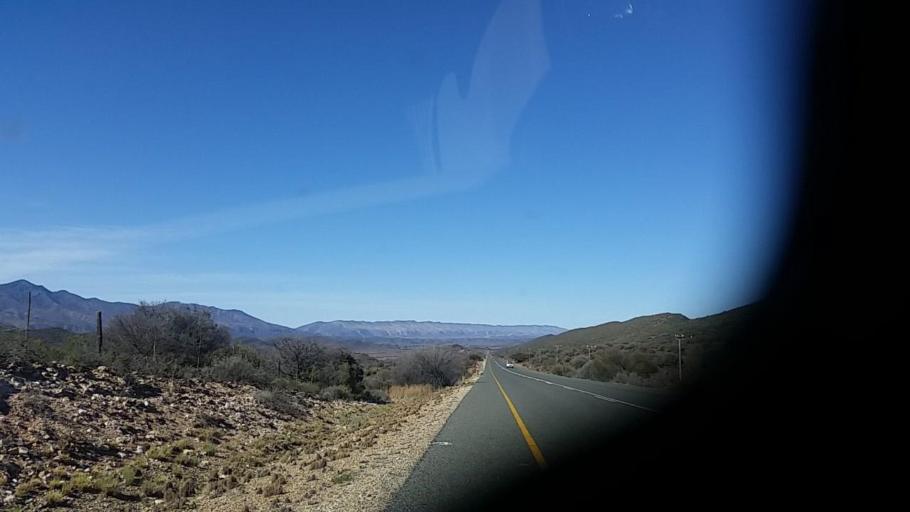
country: ZA
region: Western Cape
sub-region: Eden District Municipality
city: Knysna
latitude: -33.5225
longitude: 22.9453
